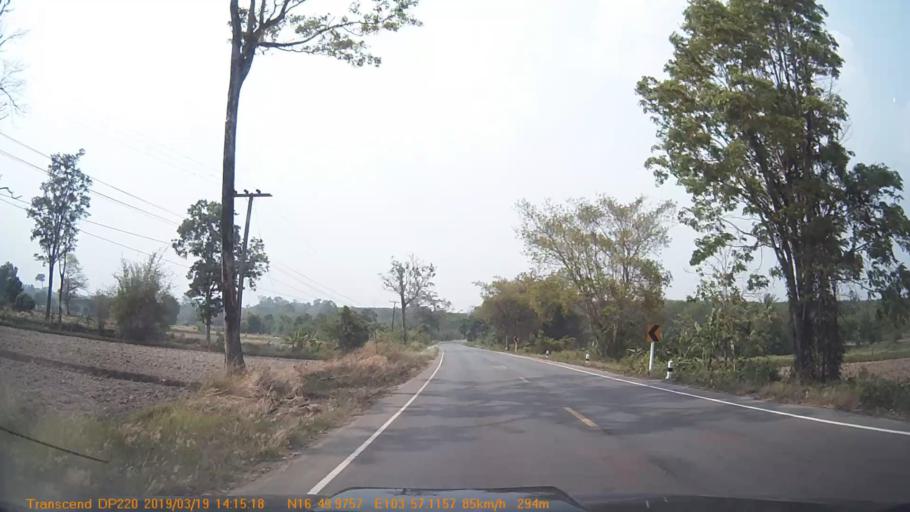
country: TH
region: Kalasin
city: Na Khu
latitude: 16.8334
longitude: 103.9515
